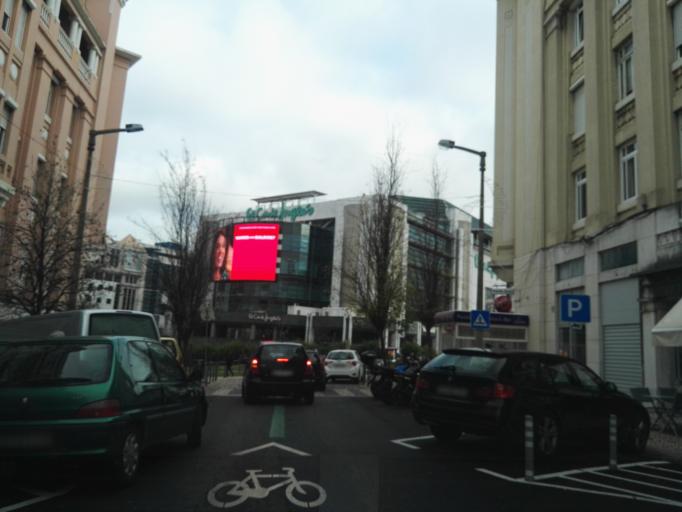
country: PT
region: Lisbon
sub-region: Lisbon
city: Lisbon
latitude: 38.7340
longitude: -9.1554
